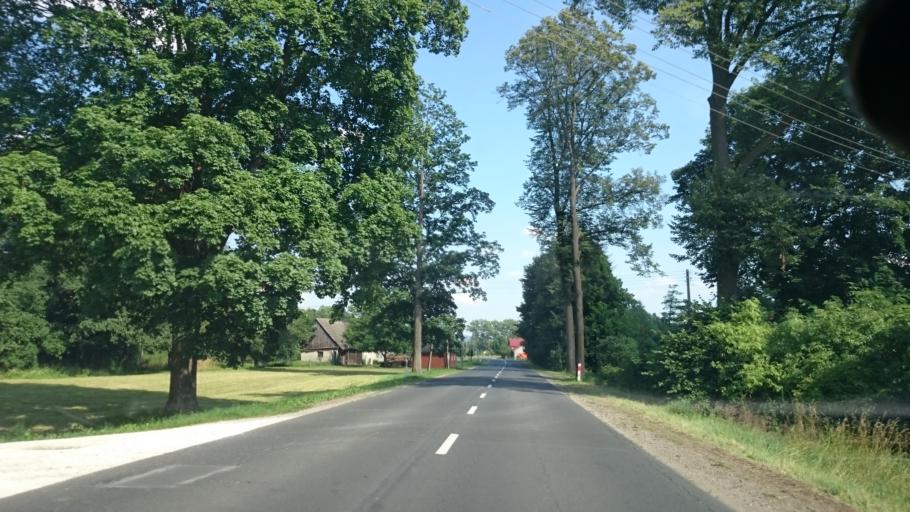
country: PL
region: Lower Silesian Voivodeship
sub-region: Powiat klodzki
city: Bystrzyca Klodzka
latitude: 50.3522
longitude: 16.7545
